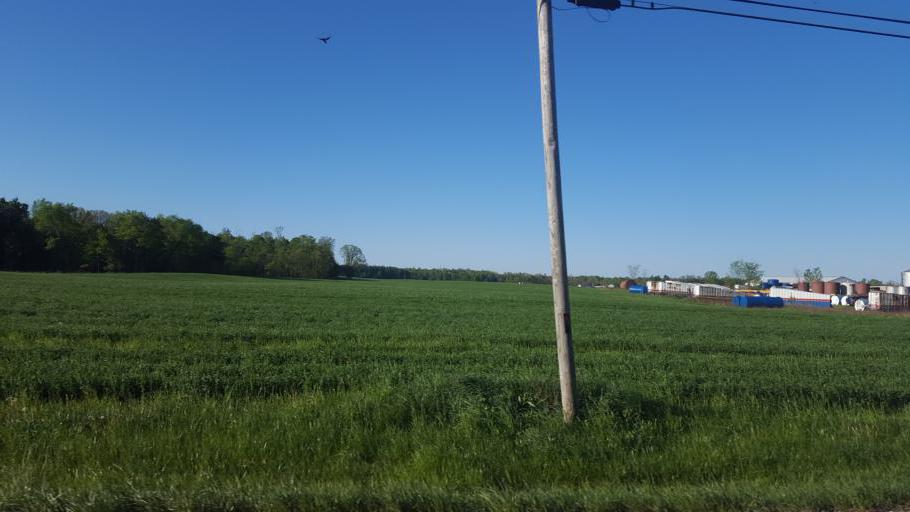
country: US
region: Ohio
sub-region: Knox County
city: Centerburg
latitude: 40.4006
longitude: -82.7711
